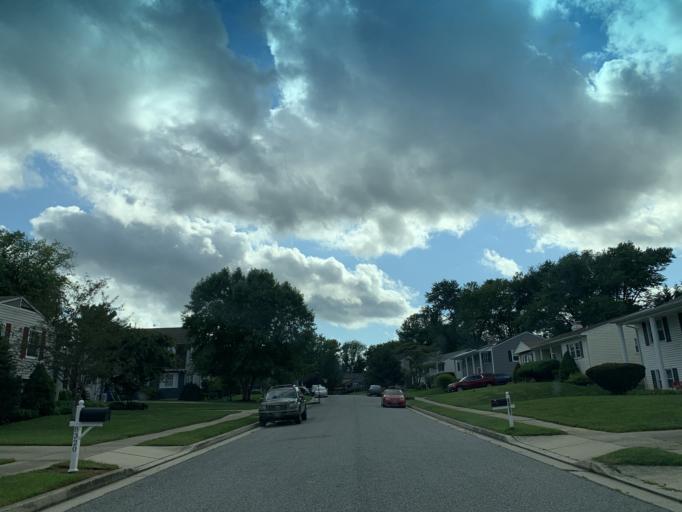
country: US
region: Maryland
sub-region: Baltimore County
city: Mays Chapel
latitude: 39.4184
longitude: -76.6531
